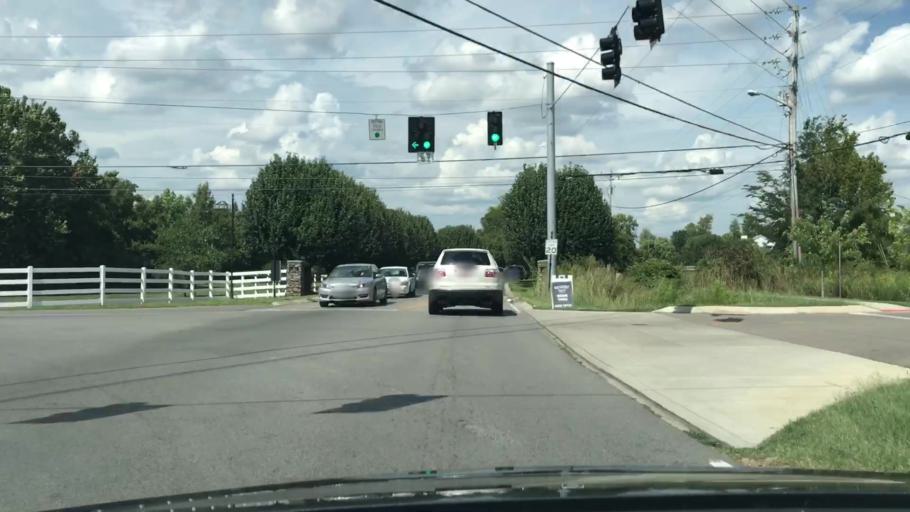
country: US
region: Tennessee
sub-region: Maury County
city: Spring Hill
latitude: 35.7444
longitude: -86.8932
